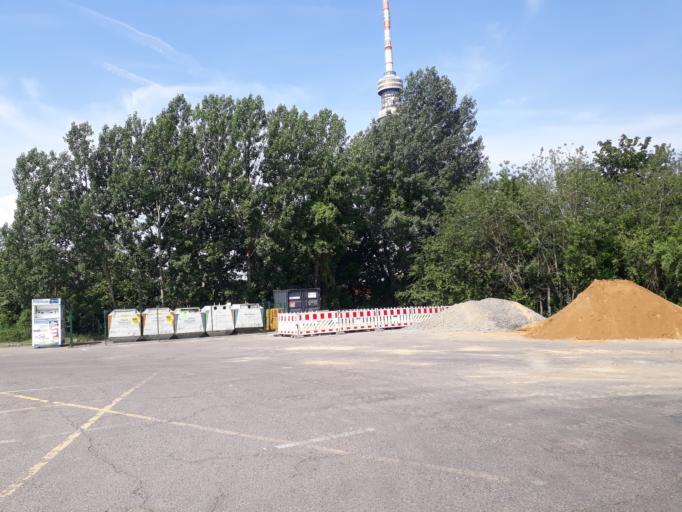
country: DE
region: Saxony
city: Heidenau
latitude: 51.0401
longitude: 13.8435
